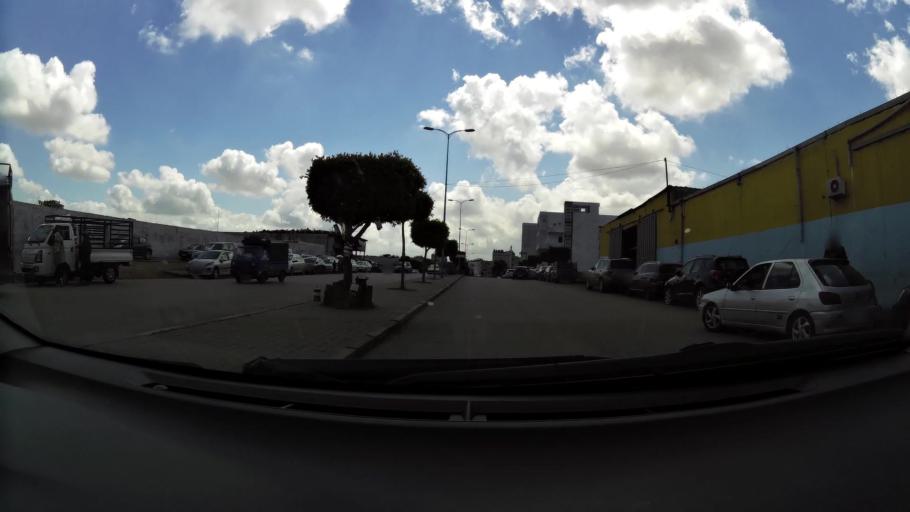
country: MA
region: Grand Casablanca
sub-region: Casablanca
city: Casablanca
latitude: 33.5412
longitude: -7.5589
